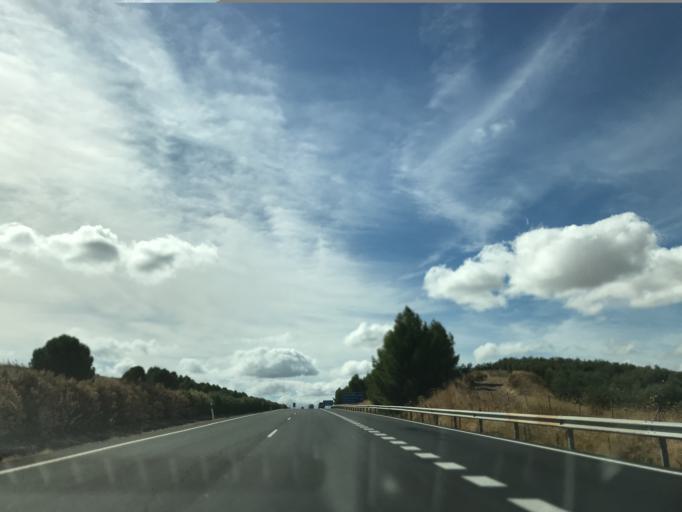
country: ES
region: Andalusia
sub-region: Province of Cordoba
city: La Victoria
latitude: 37.7248
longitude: -4.8587
